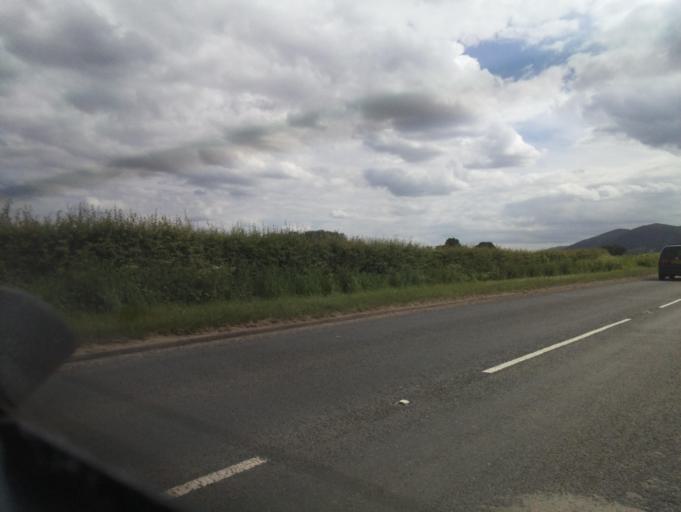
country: GB
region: England
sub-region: Worcestershire
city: Bransford
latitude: 52.1612
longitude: -2.3106
